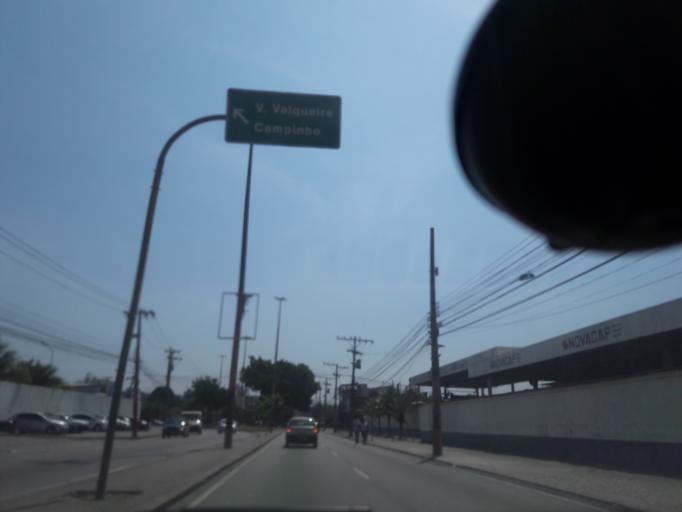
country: BR
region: Rio de Janeiro
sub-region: Sao Joao De Meriti
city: Sao Joao de Meriti
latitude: -22.8771
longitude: -43.3680
